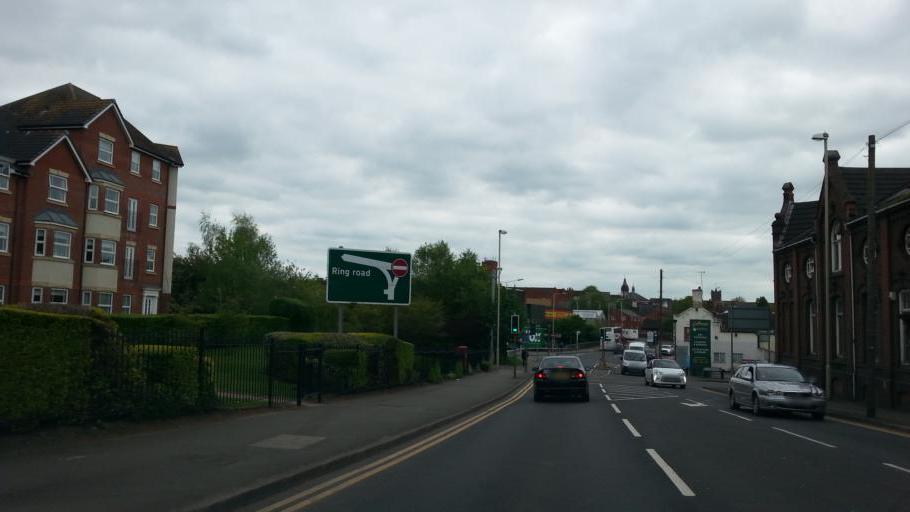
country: GB
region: England
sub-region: Dudley
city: Stourbridge
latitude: 52.4620
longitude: -2.1492
